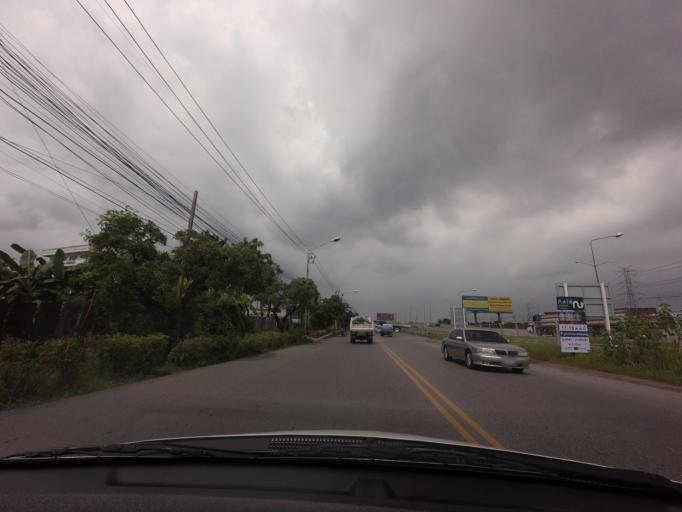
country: TH
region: Bangkok
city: Saphan Sung
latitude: 13.7457
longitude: 100.7022
